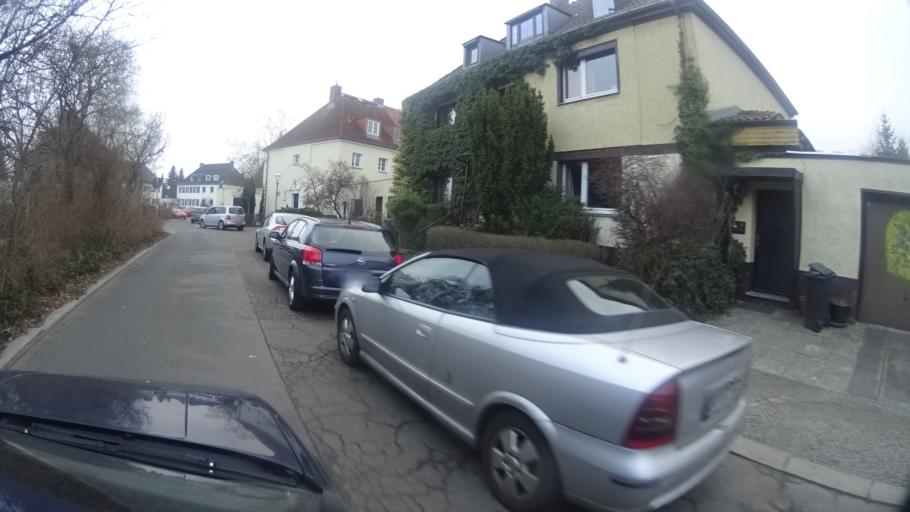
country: DE
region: Berlin
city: Tempelhof Bezirk
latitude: 52.4771
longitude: 13.3813
